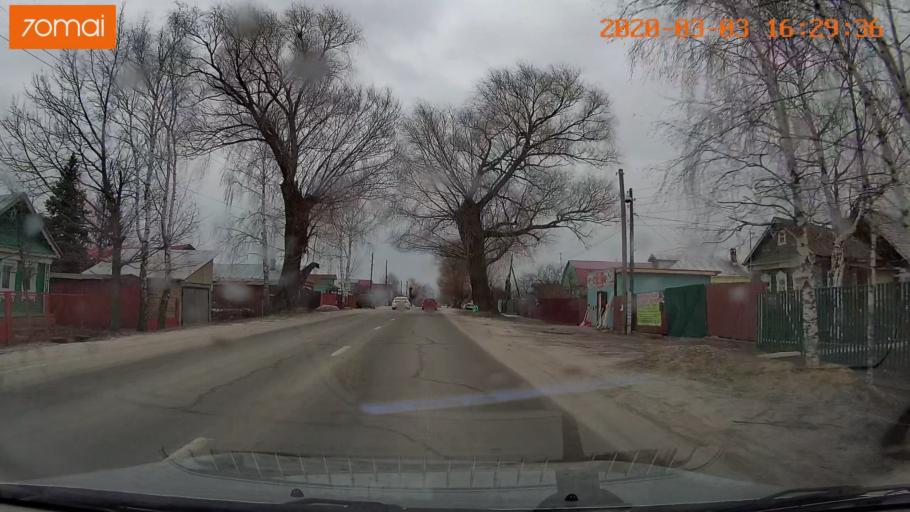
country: RU
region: Moskovskaya
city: Konobeyevo
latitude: 55.4364
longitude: 38.7023
